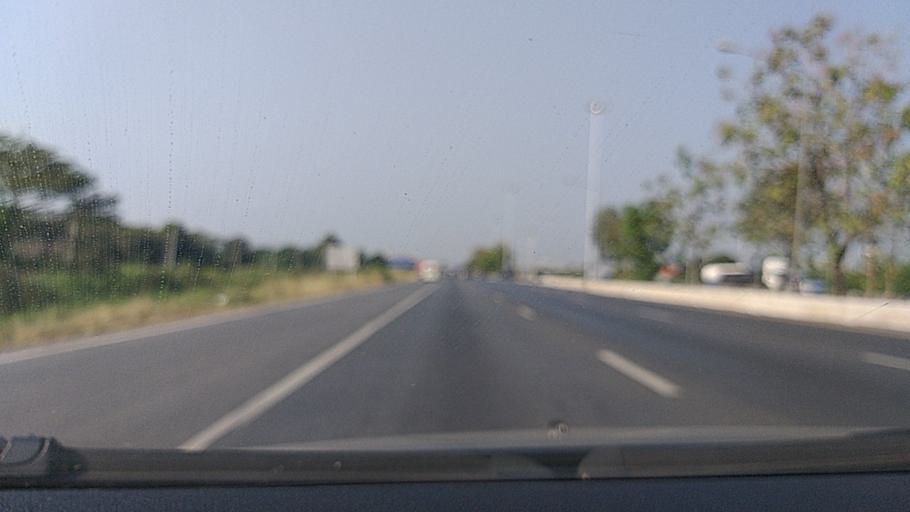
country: TH
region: Ang Thong
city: Chaiyo
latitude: 14.7195
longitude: 100.4553
